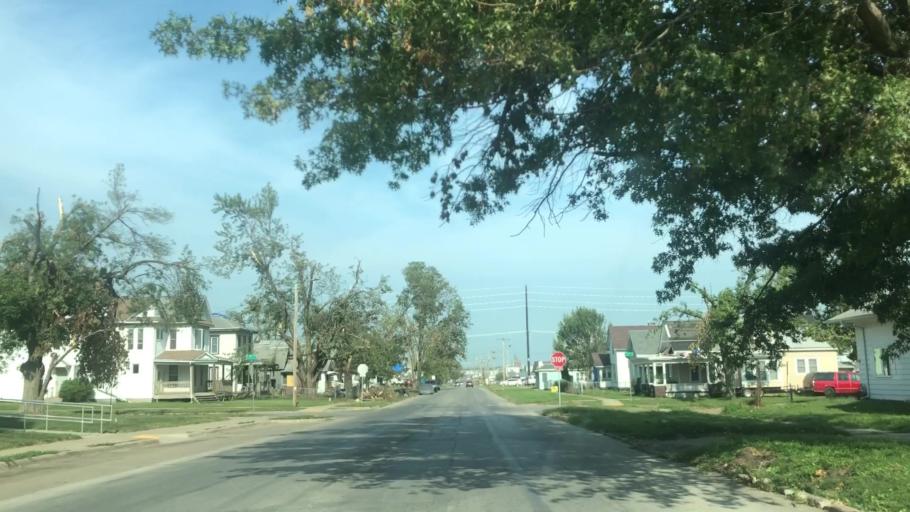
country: US
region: Iowa
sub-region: Marshall County
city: Marshalltown
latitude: 42.0492
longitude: -92.9021
